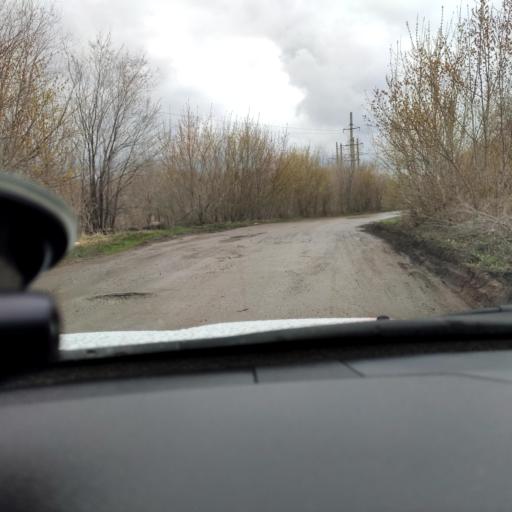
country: RU
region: Samara
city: Smyshlyayevka
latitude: 53.2643
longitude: 50.4884
